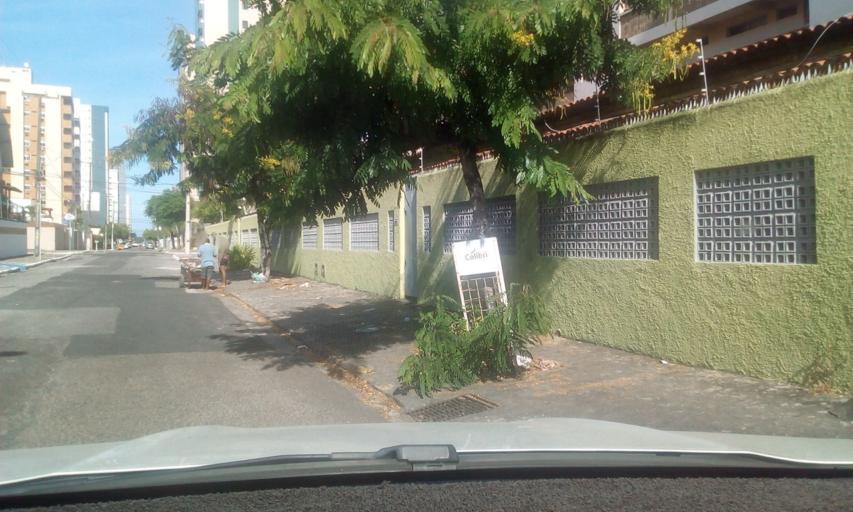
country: BR
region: Paraiba
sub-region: Joao Pessoa
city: Joao Pessoa
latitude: -7.1058
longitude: -34.8401
